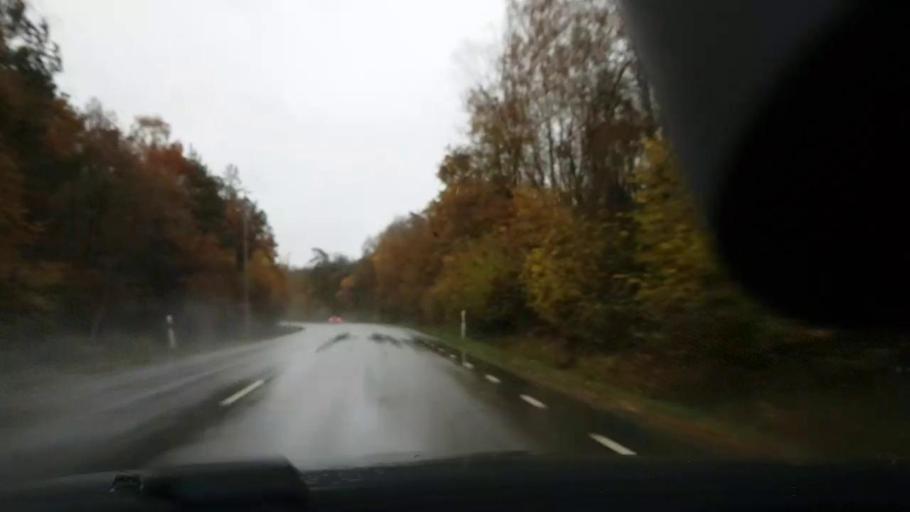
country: SE
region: Vaestra Goetaland
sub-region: Molndal
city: Kallered
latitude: 57.6029
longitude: 12.0692
